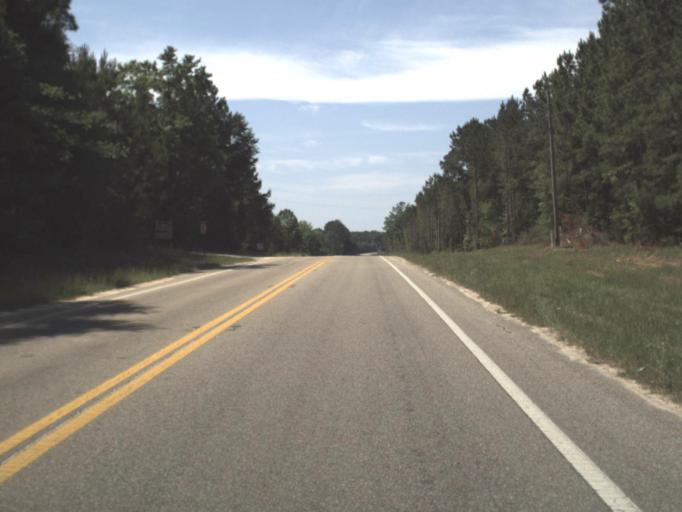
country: US
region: Florida
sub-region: Jackson County
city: Marianna
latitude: 30.7017
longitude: -85.2321
